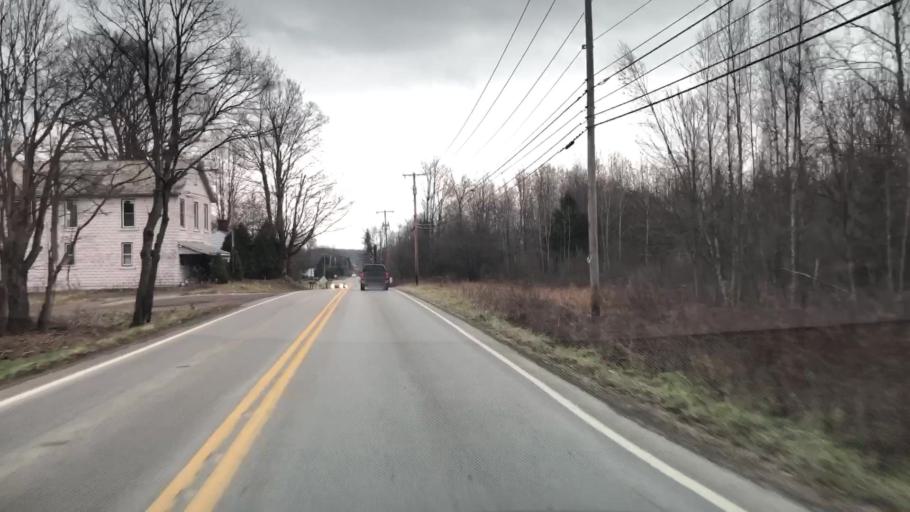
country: US
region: Pennsylvania
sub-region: Mercer County
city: Grove City
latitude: 41.1432
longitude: -80.1479
